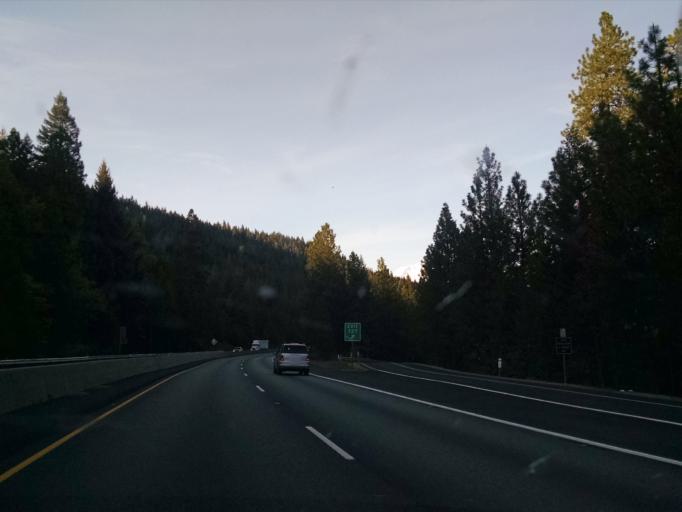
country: US
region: California
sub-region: Siskiyou County
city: Dunsmuir
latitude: 41.1706
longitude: -122.2977
